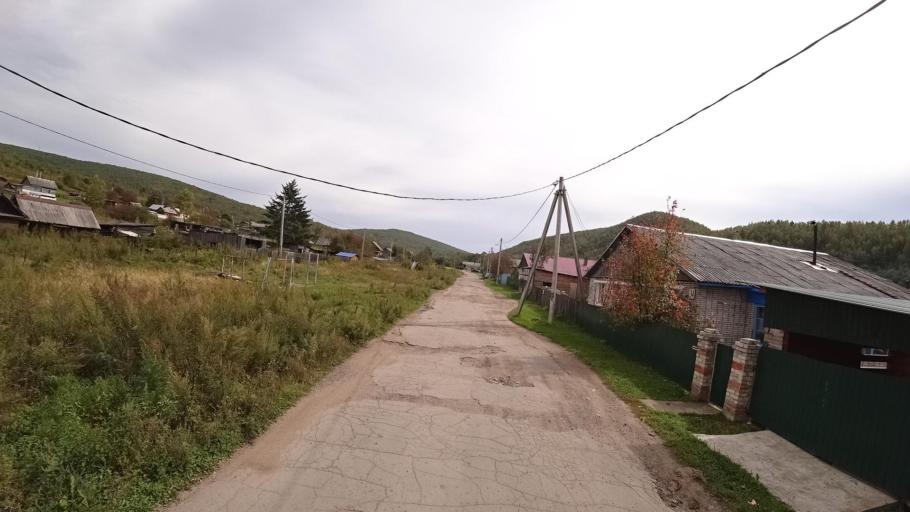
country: RU
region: Jewish Autonomous Oblast
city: Khingansk
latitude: 49.1236
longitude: 131.2040
